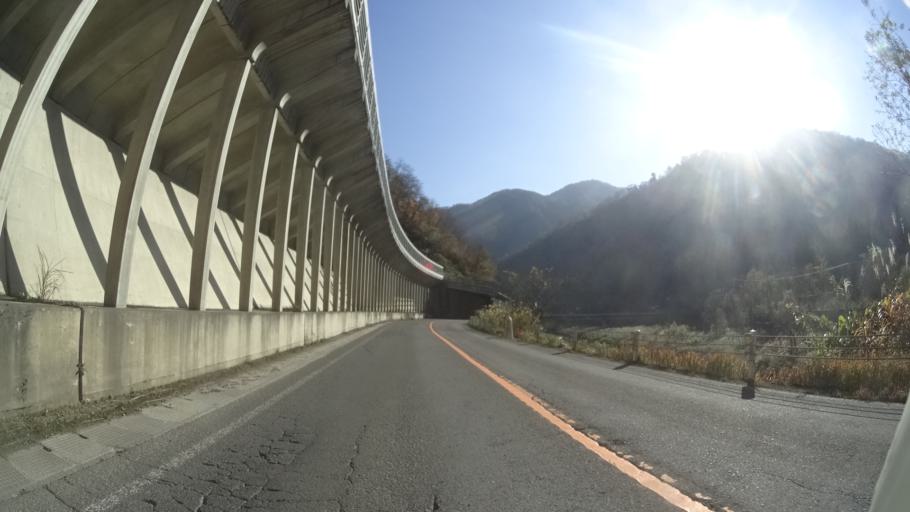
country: JP
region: Fukui
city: Ono
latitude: 35.9190
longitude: 136.6256
